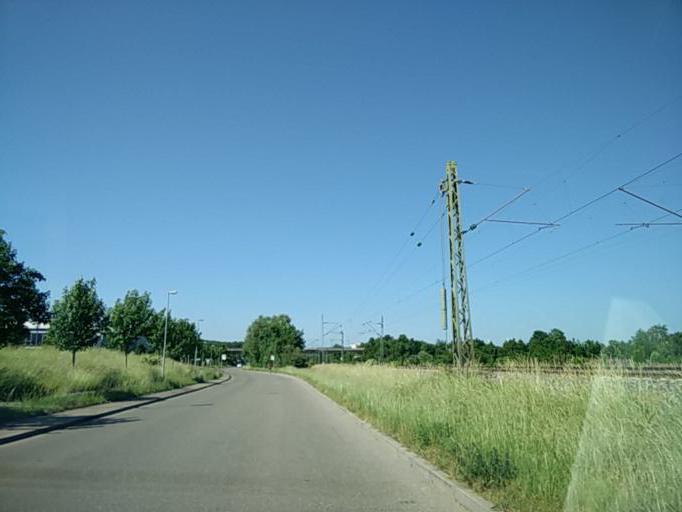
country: DE
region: Baden-Wuerttemberg
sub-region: Tuebingen Region
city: Kusterdingen
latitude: 48.5208
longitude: 9.0890
